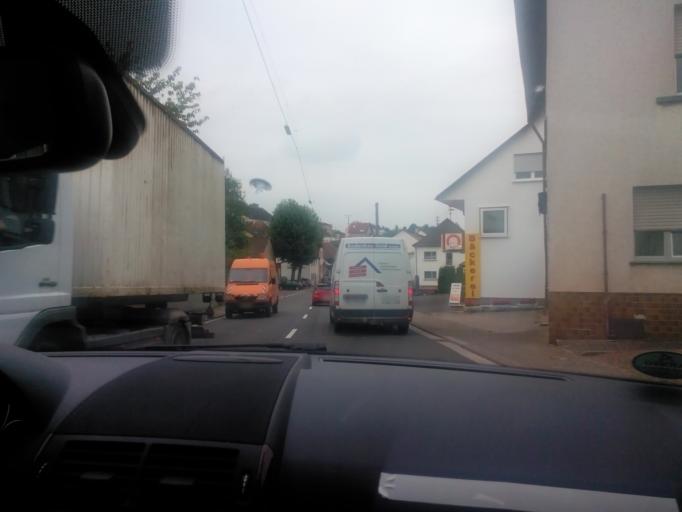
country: DE
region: Saarland
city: Lebach
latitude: 49.3884
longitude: 6.9264
